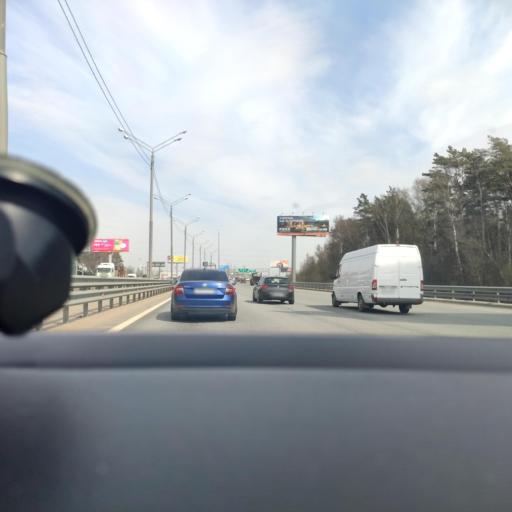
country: RU
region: Moskovskaya
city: Arkhangel'skoye
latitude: 55.8015
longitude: 37.2838
